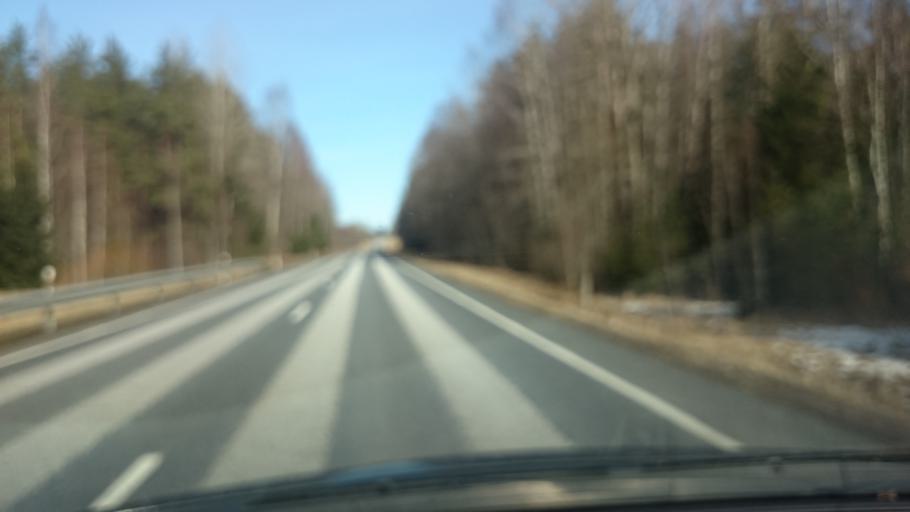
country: EE
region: Jaervamaa
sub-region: Tueri vald
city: Sarevere
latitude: 58.7442
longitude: 25.3083
